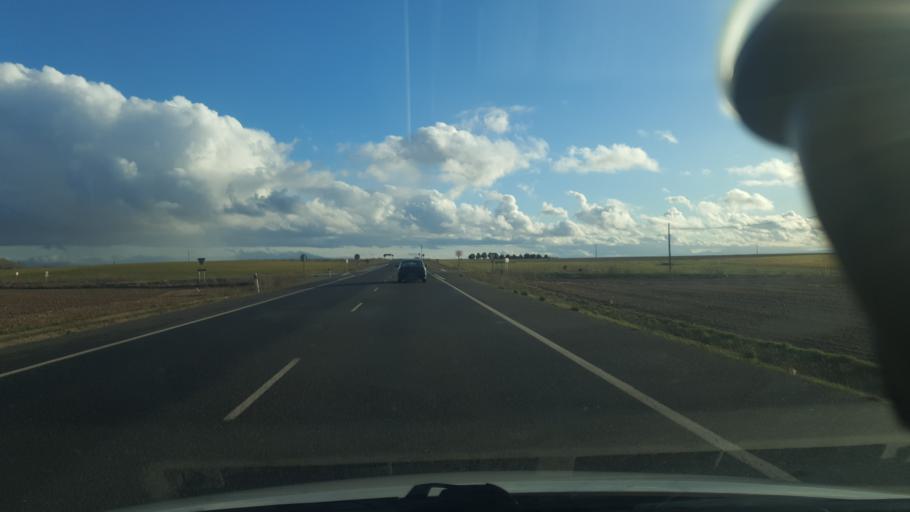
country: ES
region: Castille and Leon
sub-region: Provincia de Segovia
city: Rapariegos
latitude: 41.0914
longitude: -4.6377
